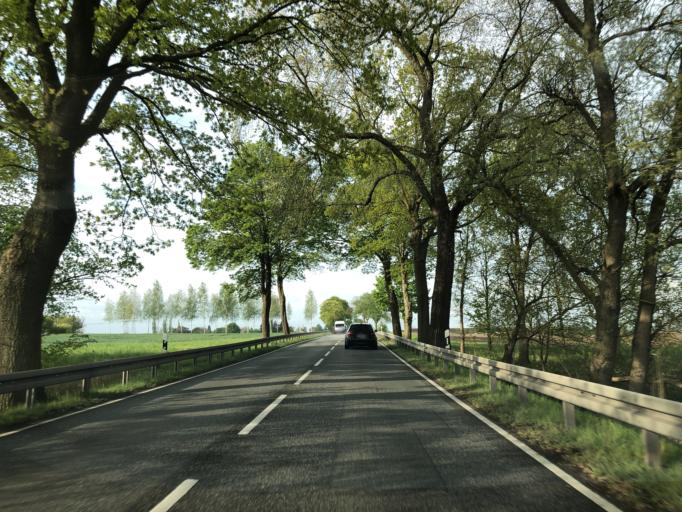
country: DE
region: Mecklenburg-Vorpommern
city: Guestrow
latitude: 53.8194
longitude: 12.1978
